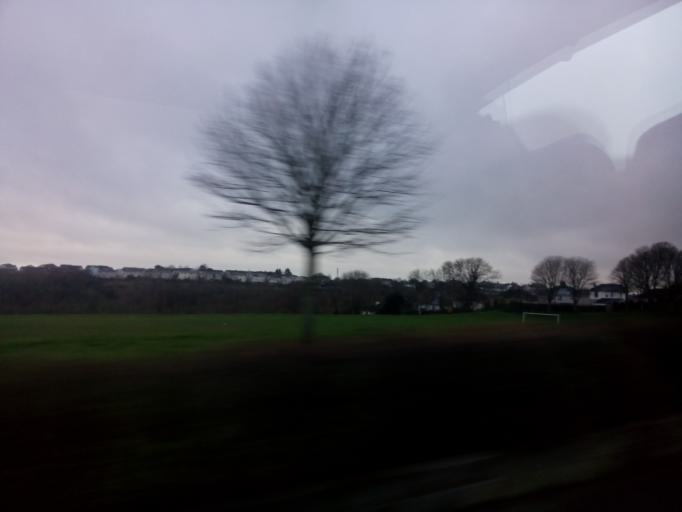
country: GB
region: England
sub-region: Cornwall
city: Torpoint
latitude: 50.4131
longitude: -4.1707
